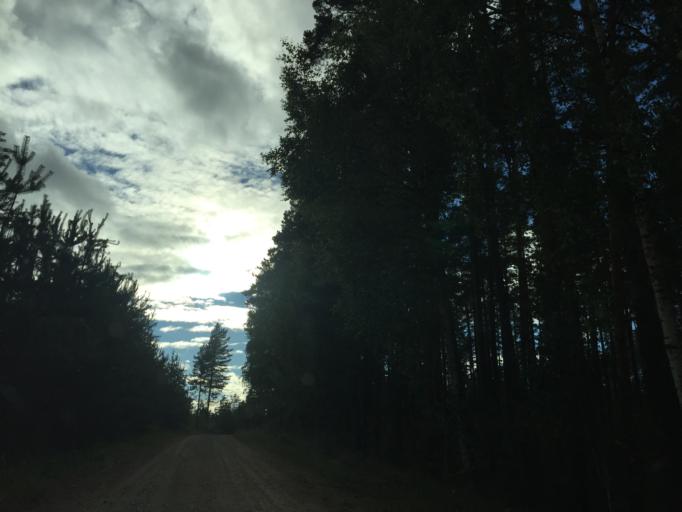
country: LV
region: Carnikava
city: Carnikava
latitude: 57.1698
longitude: 24.3596
